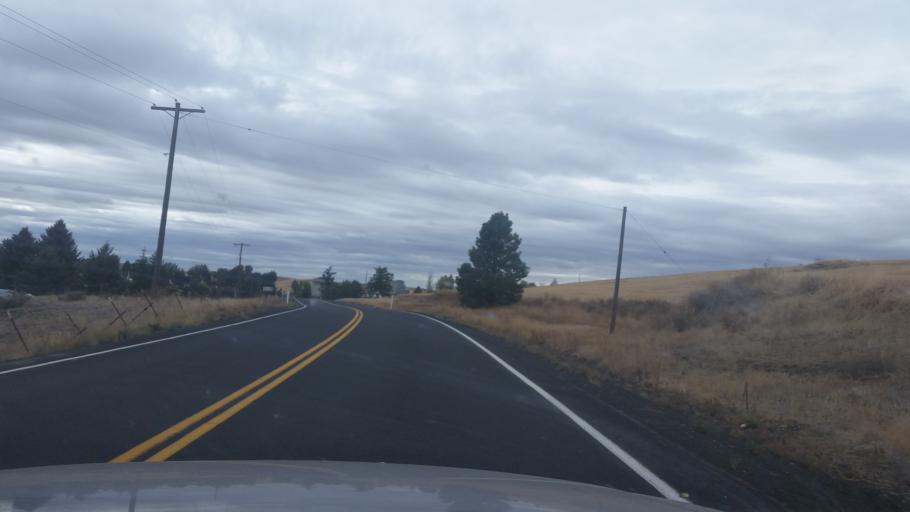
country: US
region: Washington
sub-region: Lincoln County
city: Davenport
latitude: 47.5109
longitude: -117.9457
